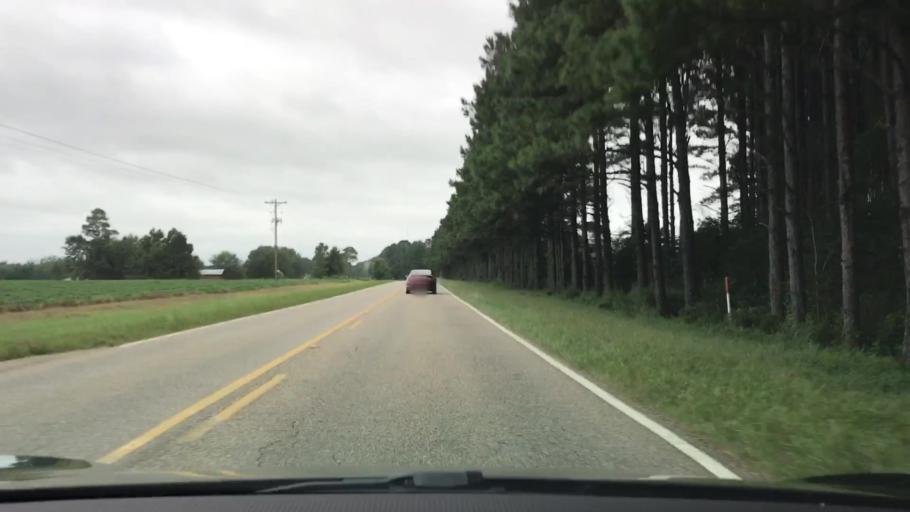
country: US
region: Alabama
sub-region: Geneva County
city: Samson
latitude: 31.1580
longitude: -86.1416
